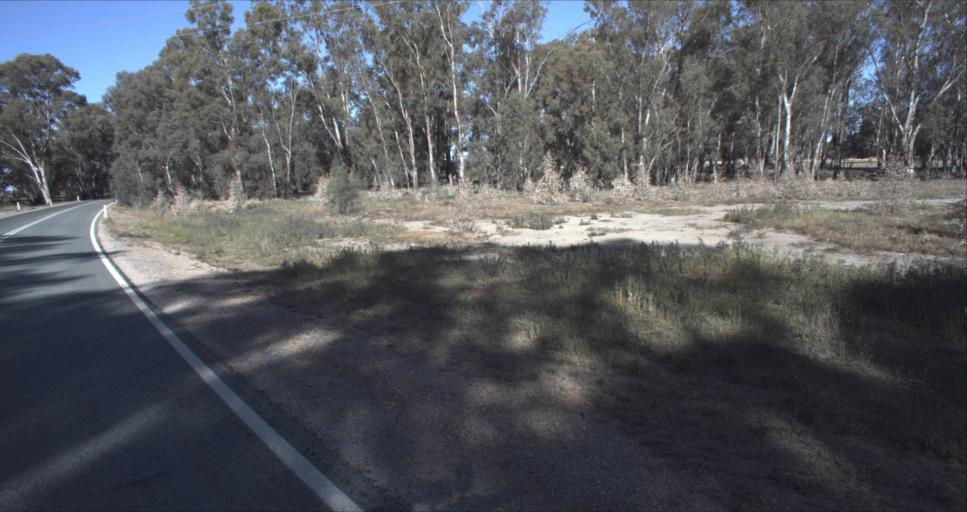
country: AU
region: New South Wales
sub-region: Leeton
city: Leeton
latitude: -34.6239
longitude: 146.3817
